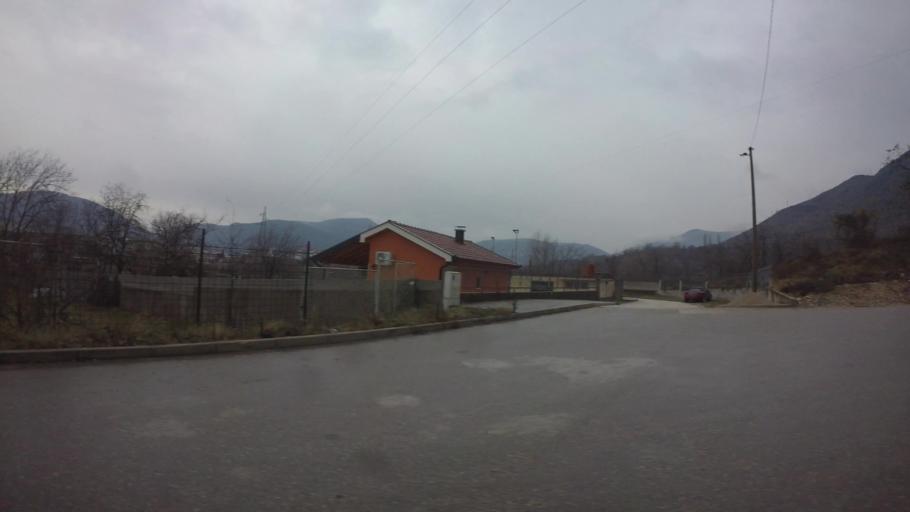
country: BA
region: Federation of Bosnia and Herzegovina
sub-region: Hercegovacko-Bosanski Kanton
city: Mostar
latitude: 43.3589
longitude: 17.7992
